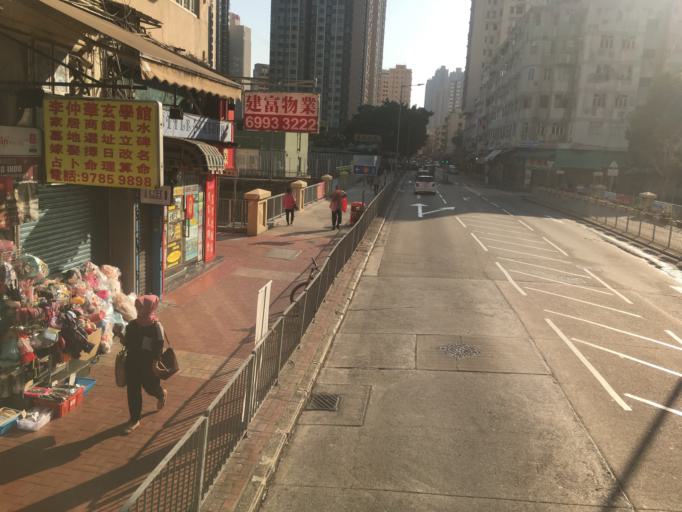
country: HK
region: Yuen Long
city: Yuen Long Kau Hui
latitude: 22.4462
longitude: 114.0253
